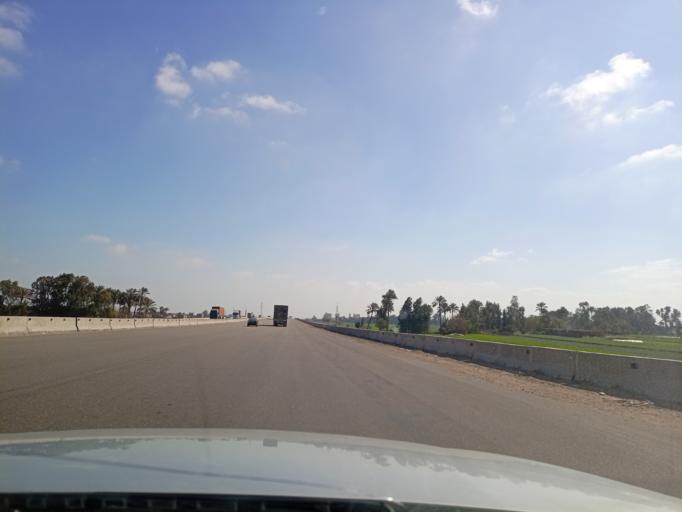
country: EG
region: Eastern Province
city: Mashtul as Suq
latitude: 30.4634
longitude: 31.3198
